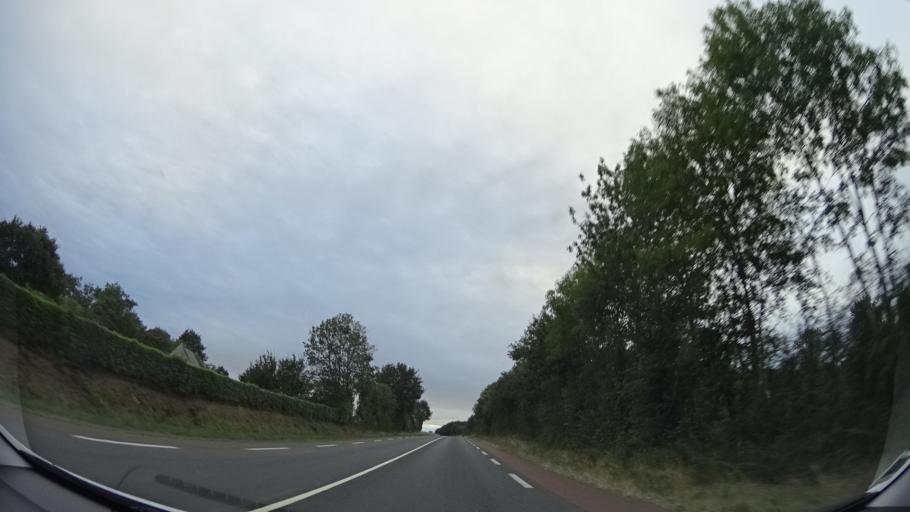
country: FR
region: Pays de la Loire
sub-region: Departement de la Sarthe
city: Loue
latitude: 48.0217
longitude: -0.1214
